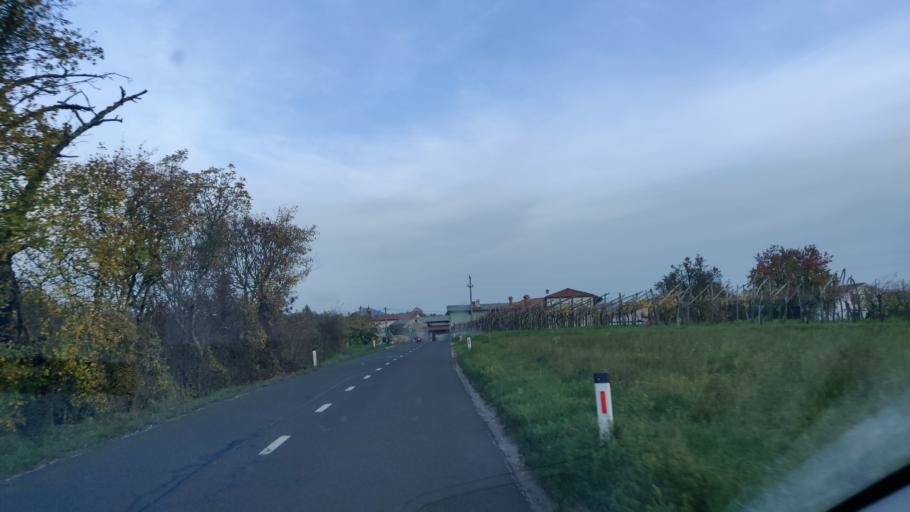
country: SI
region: Sezana
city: Sezana
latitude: 45.7622
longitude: 13.9034
